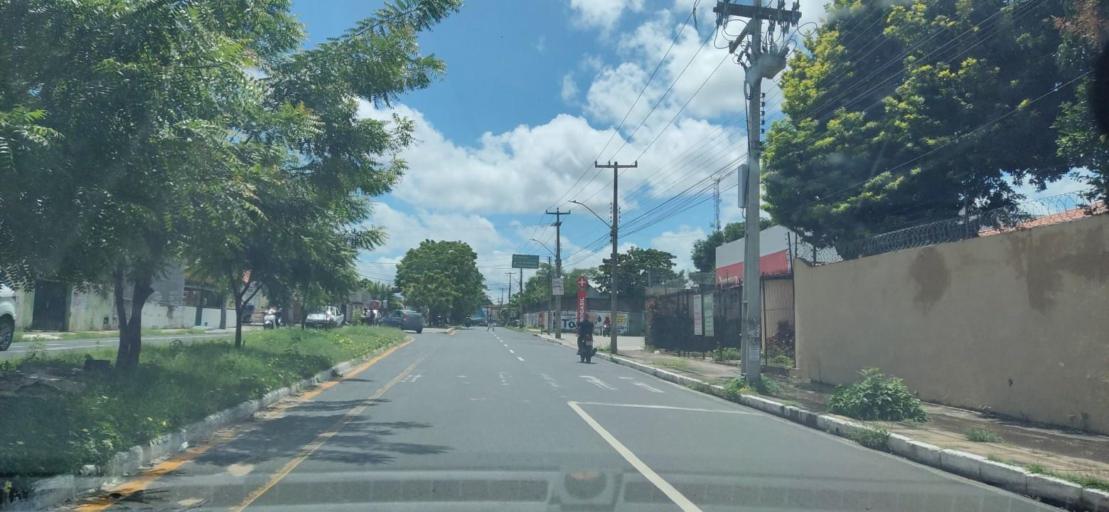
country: BR
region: Piaui
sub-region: Teresina
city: Teresina
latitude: -5.0648
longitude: -42.7634
